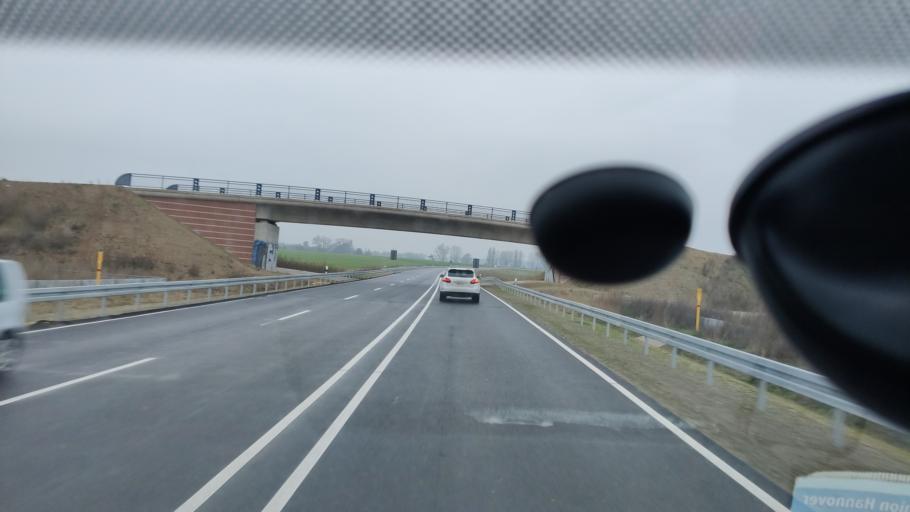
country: DE
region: Lower Saxony
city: Pattensen
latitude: 52.2887
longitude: 9.7471
